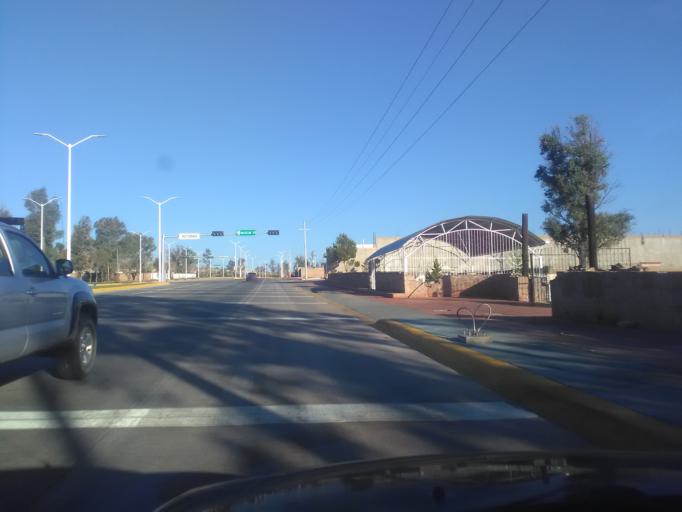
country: MX
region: Durango
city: Victoria de Durango
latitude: 23.9940
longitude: -104.7167
